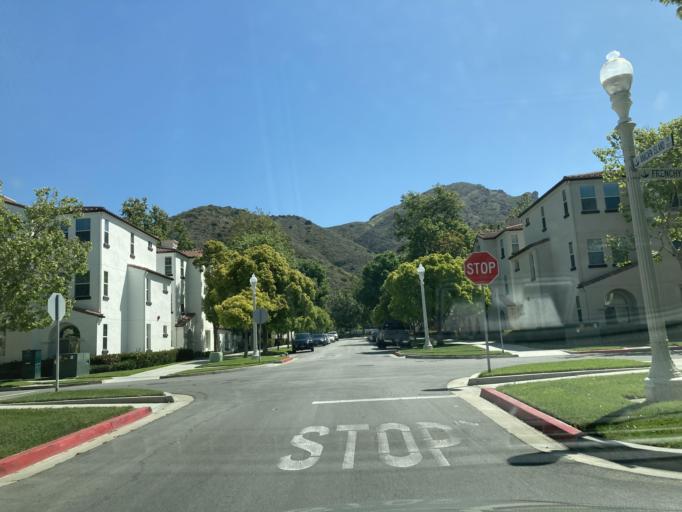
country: US
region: California
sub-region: Ventura County
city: Camarillo
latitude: 34.1641
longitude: -119.0353
